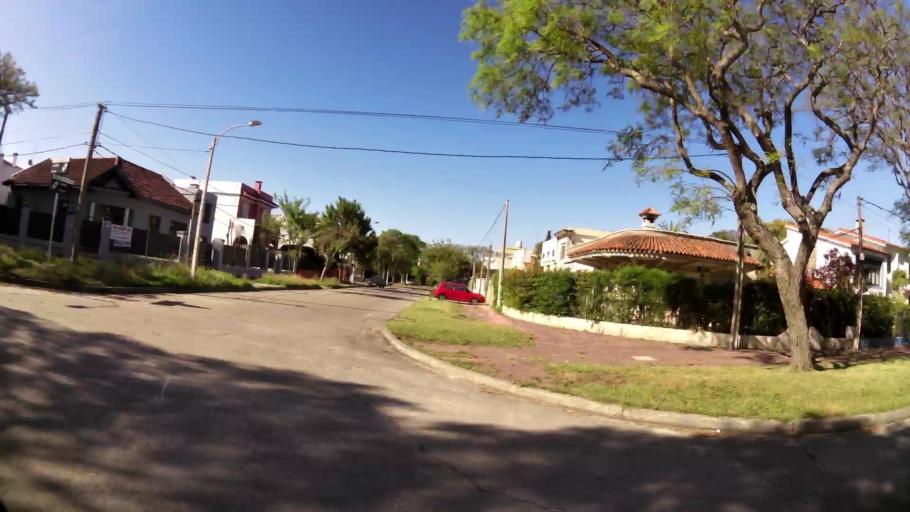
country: UY
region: Canelones
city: Paso de Carrasco
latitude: -34.8946
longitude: -56.0619
